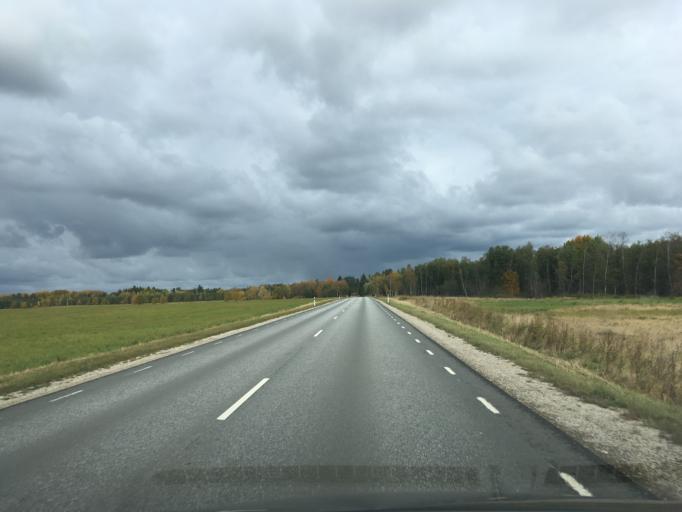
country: EE
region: Harju
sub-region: Anija vald
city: Kehra
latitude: 59.2857
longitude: 25.3747
